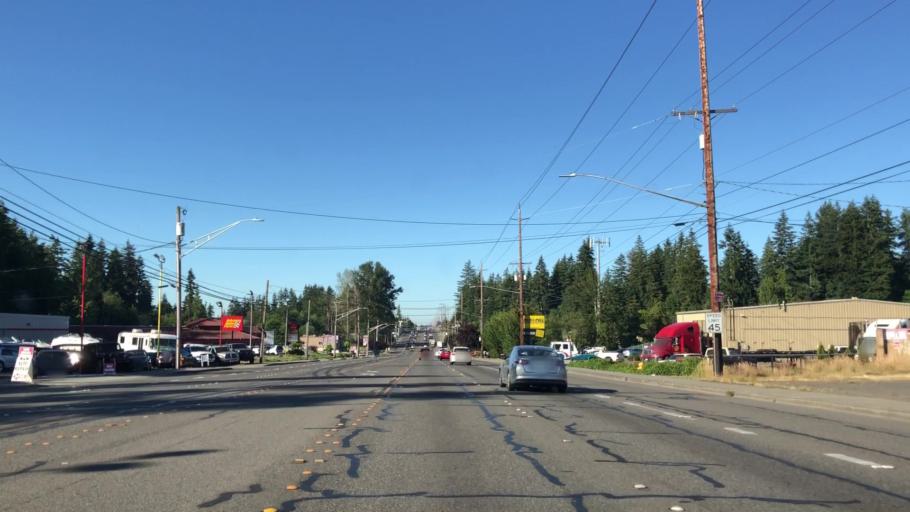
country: US
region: Washington
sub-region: Snohomish County
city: Lynnwood
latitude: 47.8341
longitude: -122.3047
